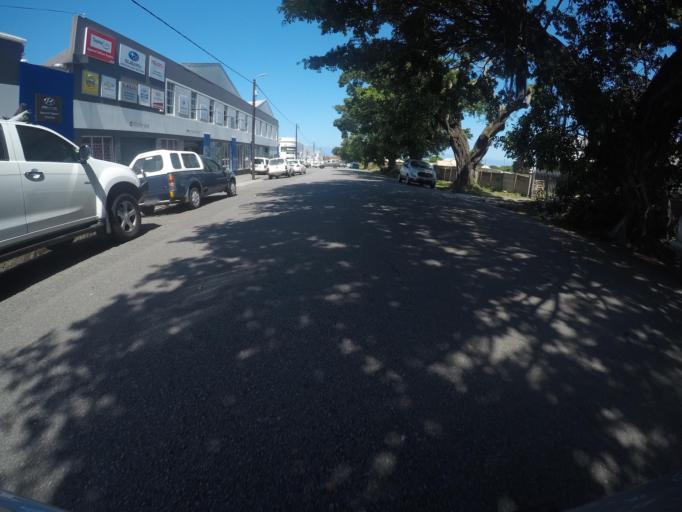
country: ZA
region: Eastern Cape
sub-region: Buffalo City Metropolitan Municipality
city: East London
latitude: -33.0095
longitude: 27.9047
